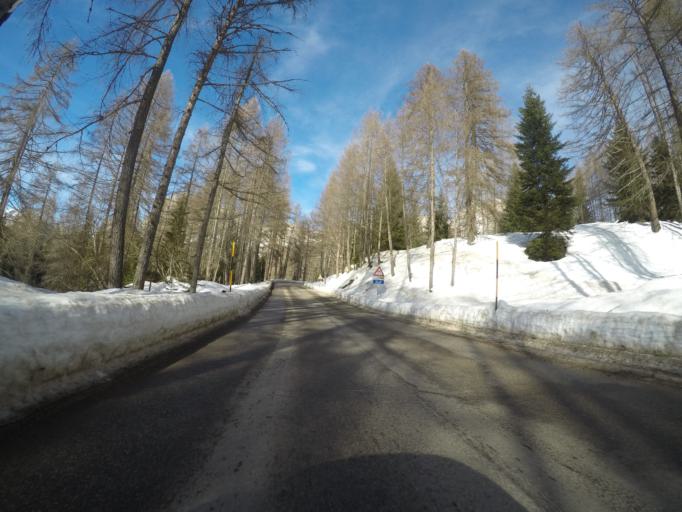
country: IT
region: Veneto
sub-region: Provincia di Belluno
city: Cortina d'Ampezzo
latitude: 46.5434
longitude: 12.1634
